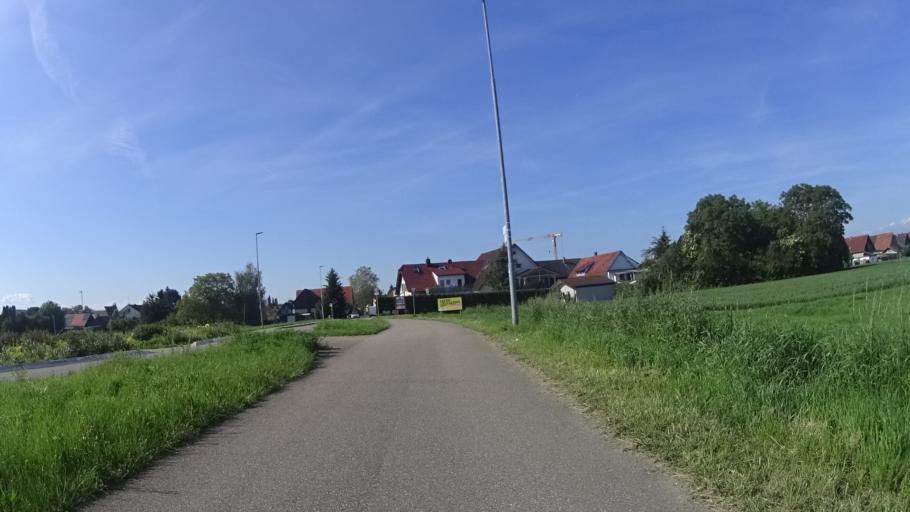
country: DE
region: Baden-Wuerttemberg
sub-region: Freiburg Region
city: Kehl
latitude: 48.5252
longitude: 7.8253
